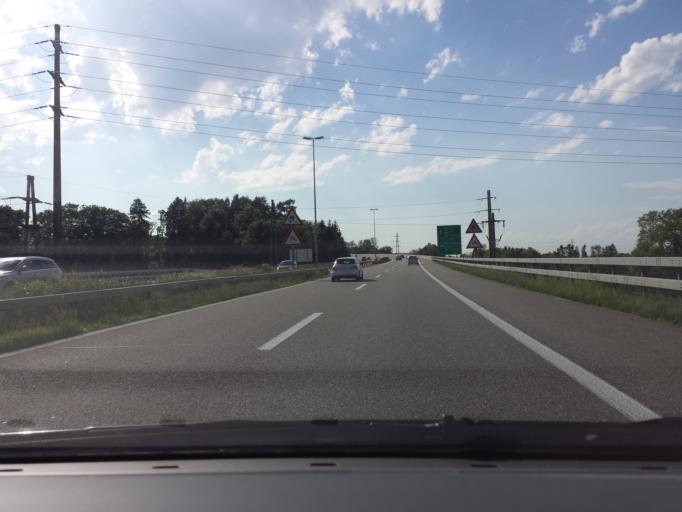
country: CH
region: Saint Gallen
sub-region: Wahlkreis Rorschach
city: Goldach
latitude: 47.4677
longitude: 9.4582
